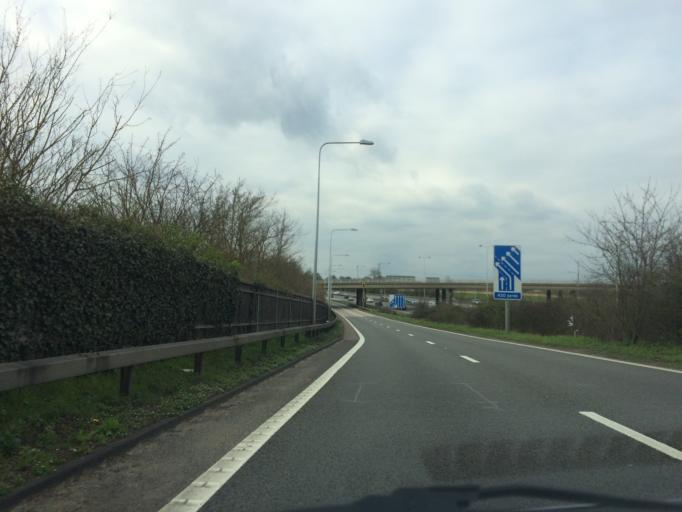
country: GB
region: England
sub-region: Surrey
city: Chertsey
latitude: 51.3760
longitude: -0.5103
